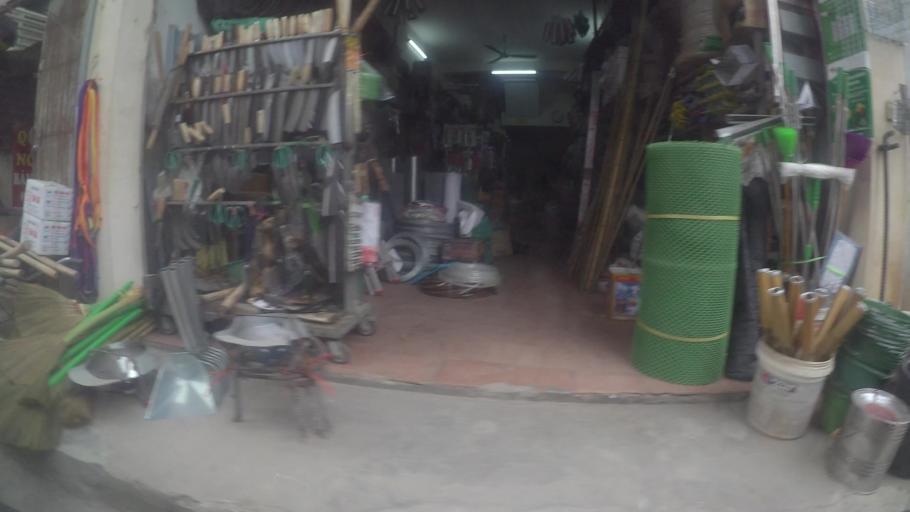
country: VN
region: Ha Noi
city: Cau Dien
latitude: 21.0347
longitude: 105.7406
